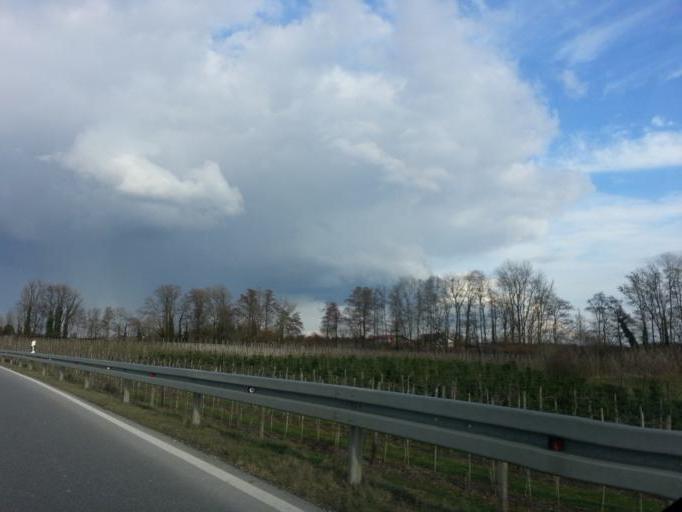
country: DE
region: Baden-Wuerttemberg
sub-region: Tuebingen Region
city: Immenstaad am Bodensee
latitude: 47.6842
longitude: 9.3919
